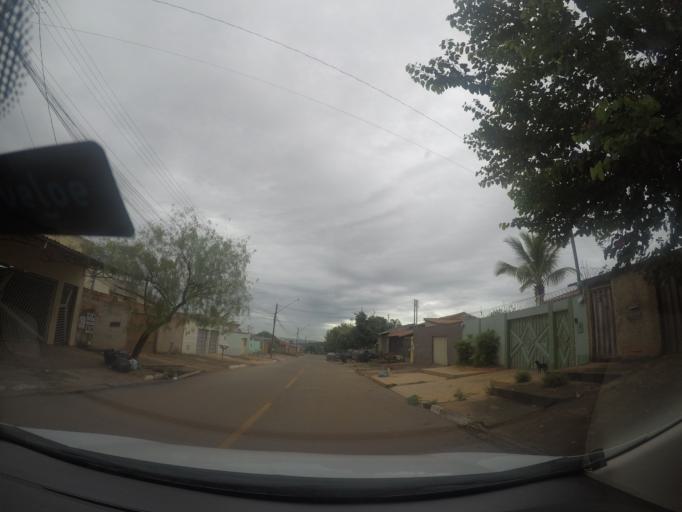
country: BR
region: Goias
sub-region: Goiania
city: Goiania
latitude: -16.6122
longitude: -49.3094
